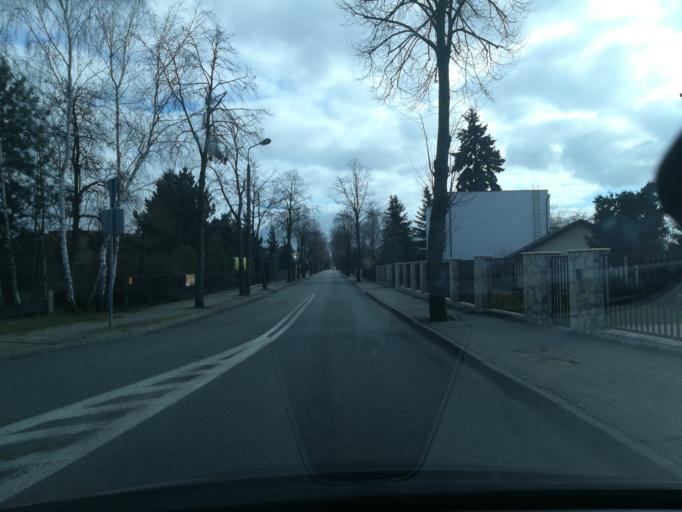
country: PL
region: Kujawsko-Pomorskie
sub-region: Powiat aleksandrowski
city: Ciechocinek
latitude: 52.8750
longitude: 18.7752
